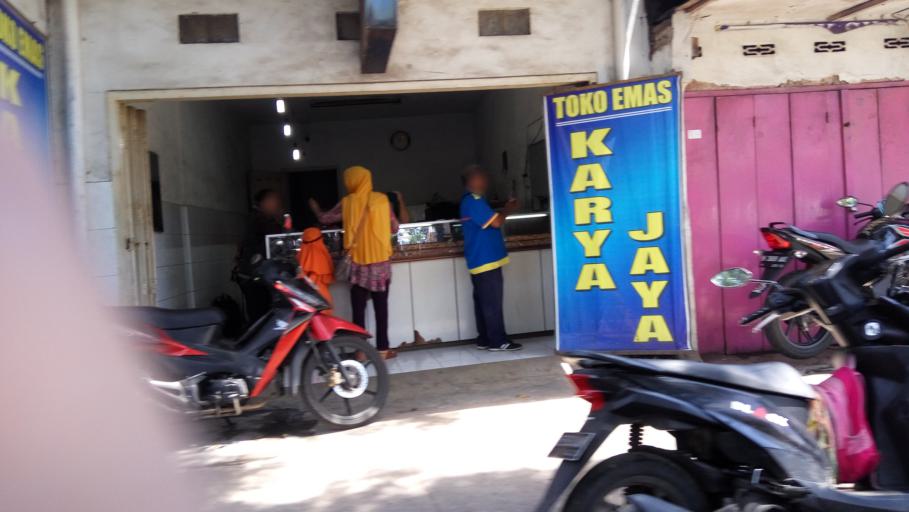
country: ID
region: East Java
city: Malang
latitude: -7.9401
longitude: 112.6387
